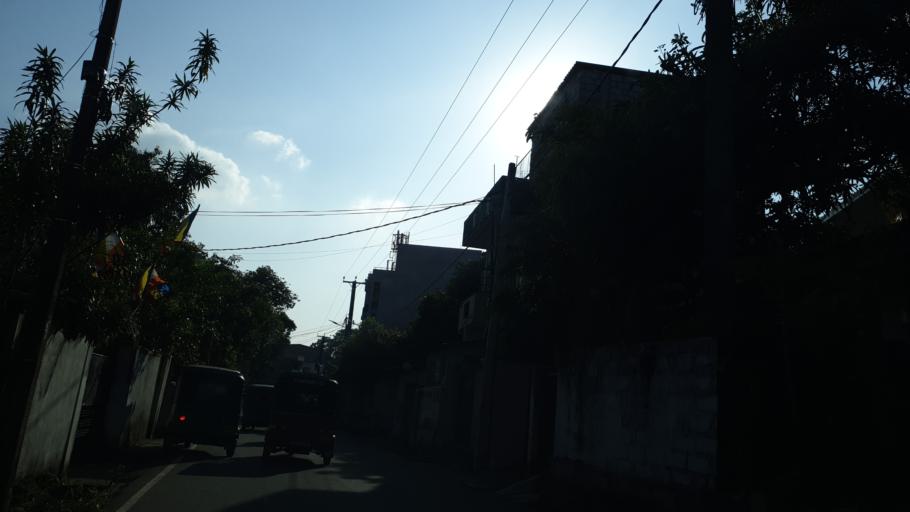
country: LK
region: Western
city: Galkissa
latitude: 6.8512
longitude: 79.8808
